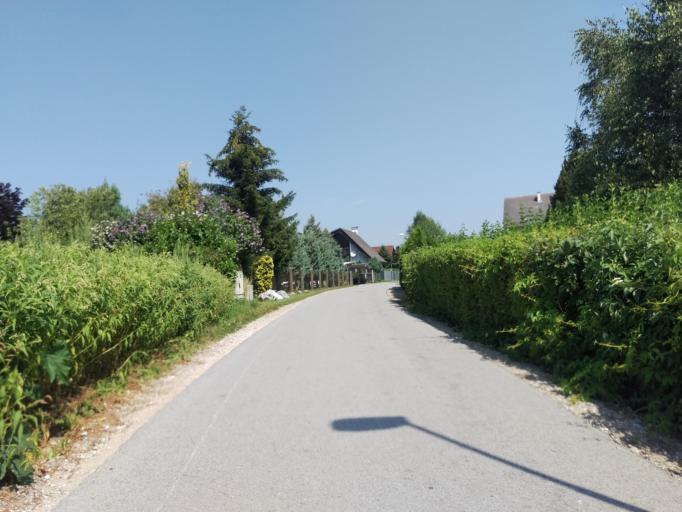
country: AT
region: Styria
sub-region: Politischer Bezirk Graz-Umgebung
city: Werndorf
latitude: 46.9386
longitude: 15.4871
